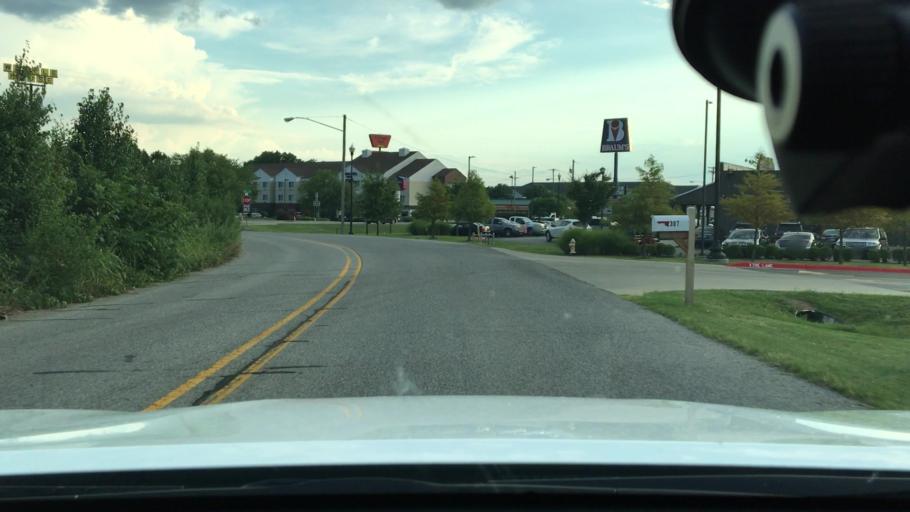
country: US
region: Arkansas
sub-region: Benton County
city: Bentonville
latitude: 36.3358
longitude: -94.1850
